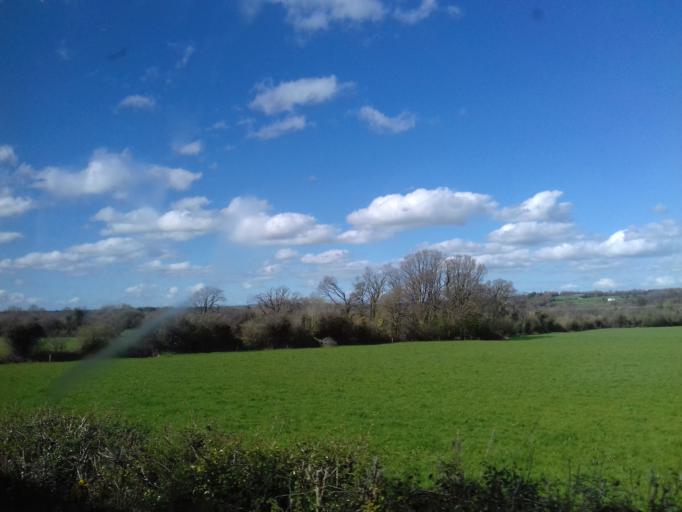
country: IE
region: Munster
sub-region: County Cork
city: Kanturk
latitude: 52.1249
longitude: -8.8172
